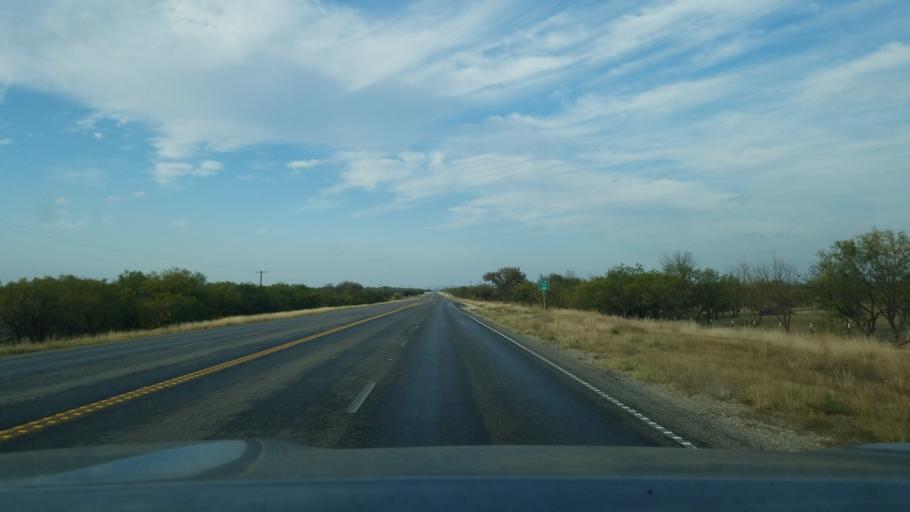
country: US
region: Texas
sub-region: Brown County
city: Early
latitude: 31.7821
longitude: -98.9475
